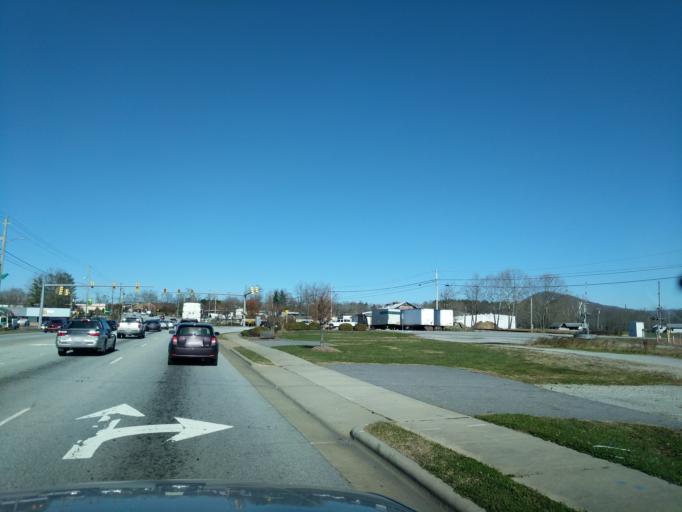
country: US
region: North Carolina
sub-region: Henderson County
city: Fletcher
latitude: 35.4273
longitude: -82.5020
